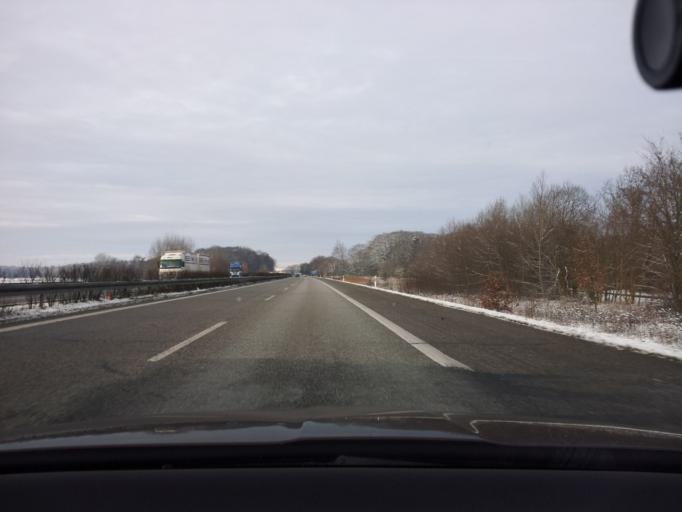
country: DE
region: Mecklenburg-Vorpommern
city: Wittenburg
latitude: 53.4932
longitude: 11.1484
